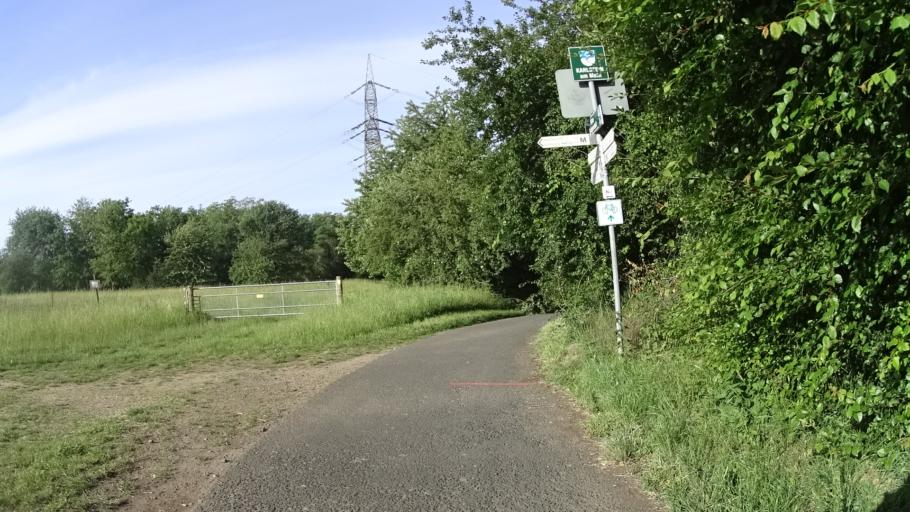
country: DE
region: Bavaria
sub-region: Regierungsbezirk Unterfranken
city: Kahl am Main
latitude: 50.0627
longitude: 8.9893
